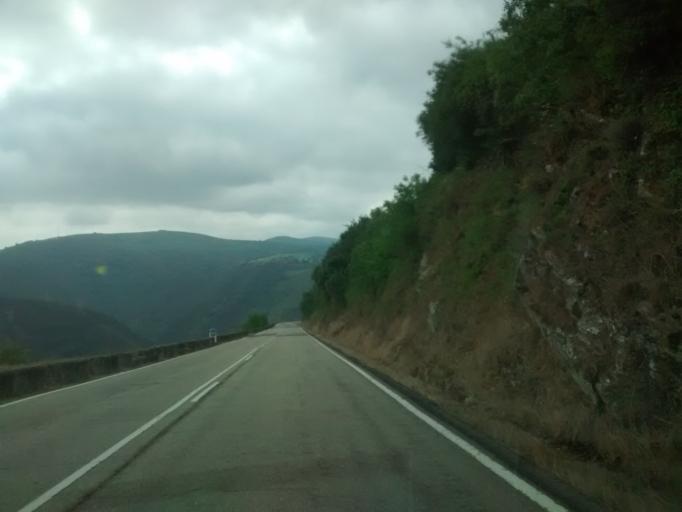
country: ES
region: Galicia
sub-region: Provincia de Ourense
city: Manzaneda
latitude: 42.3338
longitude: -7.2198
